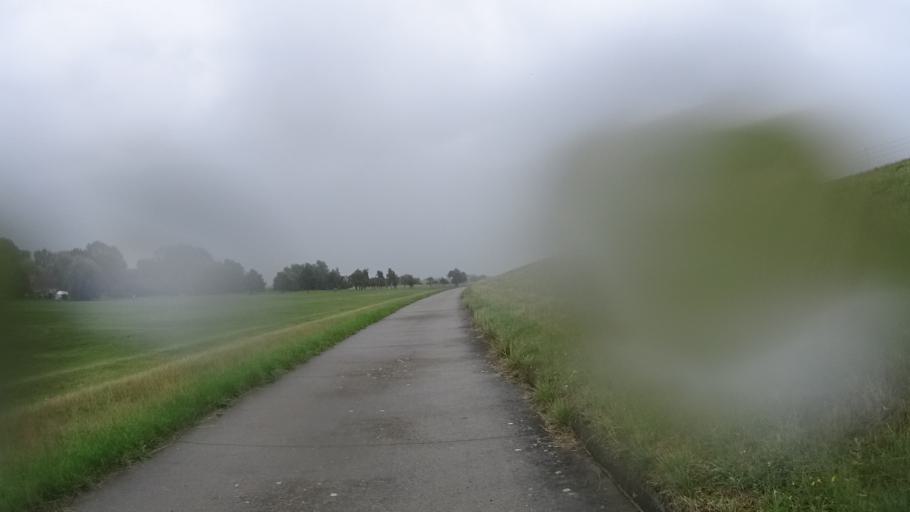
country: DE
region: Lower Saxony
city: Hitzacker
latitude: 53.1824
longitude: 11.0171
